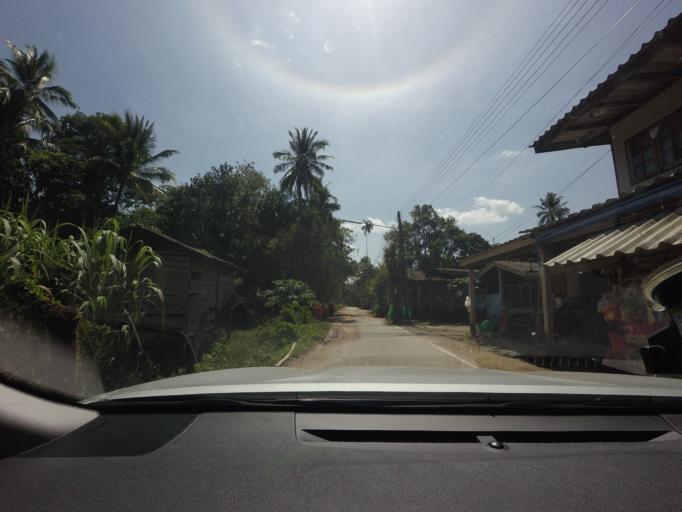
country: TH
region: Narathiwat
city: Rueso
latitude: 6.3839
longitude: 101.5190
